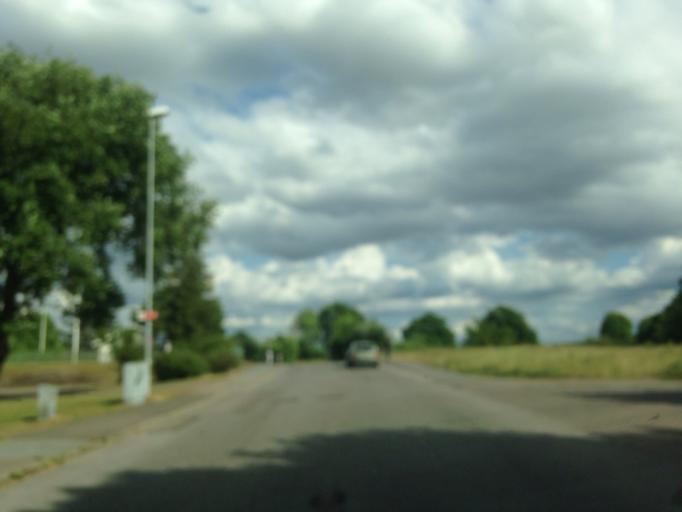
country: SE
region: Vaestra Goetaland
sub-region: Goteborg
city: Majorna
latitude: 57.7537
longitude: 11.9240
